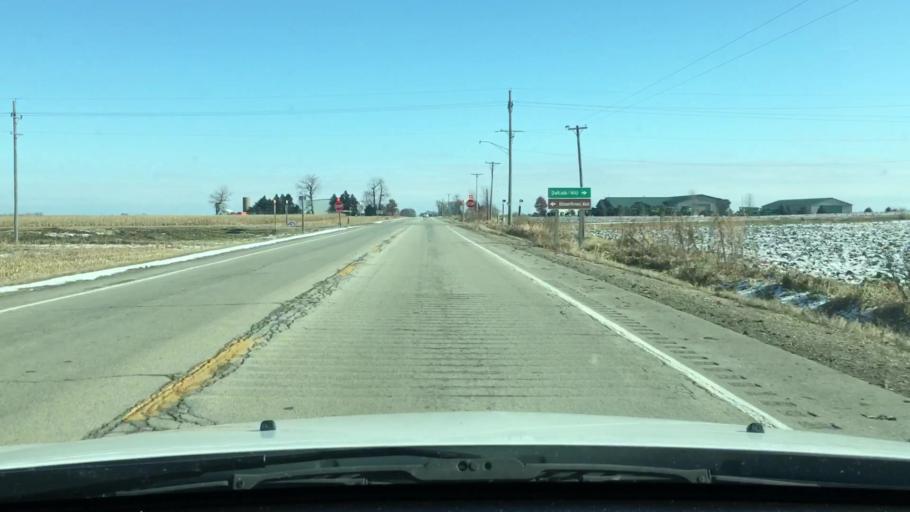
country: US
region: Illinois
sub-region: DeKalb County
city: DeKalb
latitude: 42.0016
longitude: -88.7842
